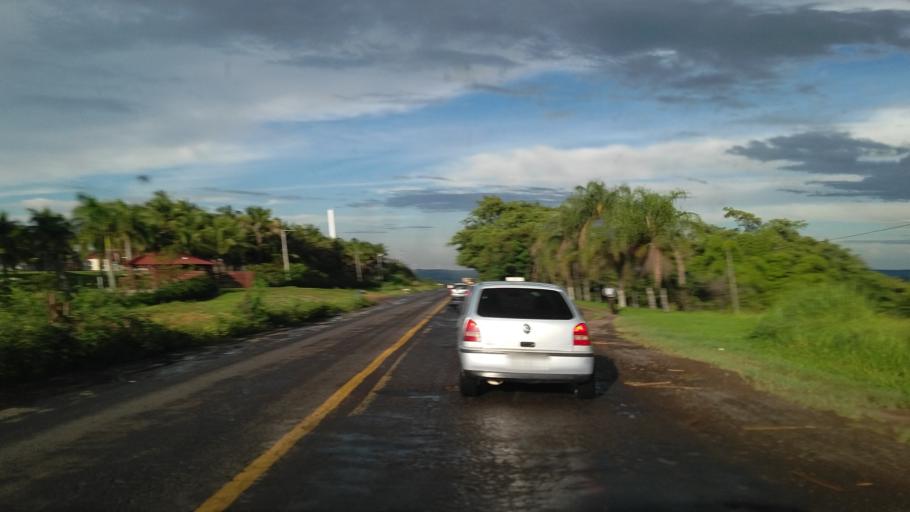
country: BR
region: Sao Paulo
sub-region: Marilia
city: Marilia
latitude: -22.1295
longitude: -49.9398
